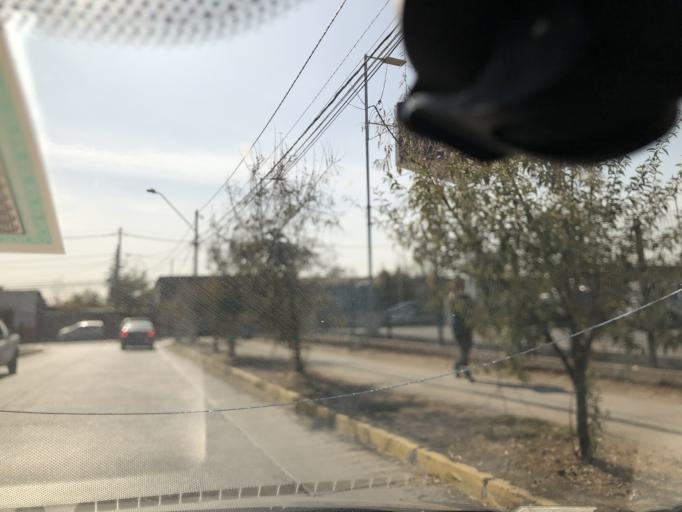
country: CL
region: Santiago Metropolitan
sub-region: Provincia de Cordillera
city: Puente Alto
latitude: -33.6135
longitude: -70.5798
